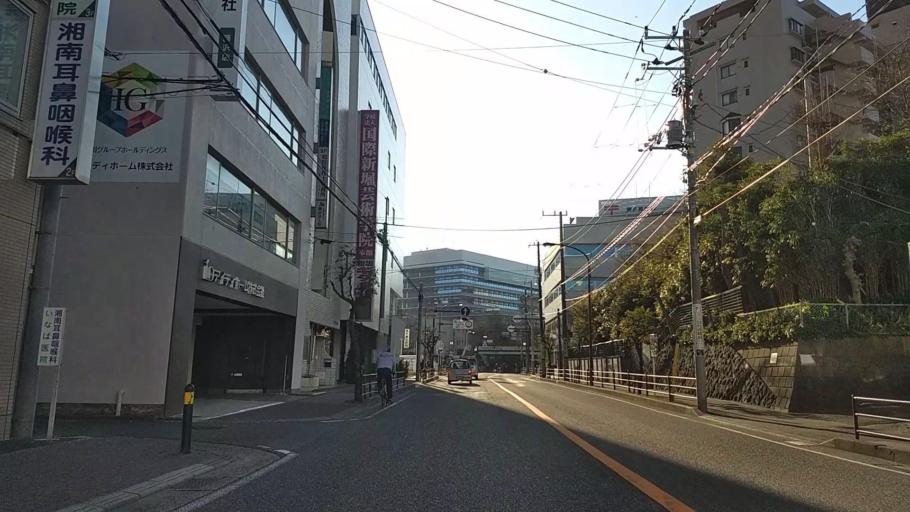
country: JP
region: Kanagawa
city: Fujisawa
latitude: 35.3411
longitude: 139.4894
